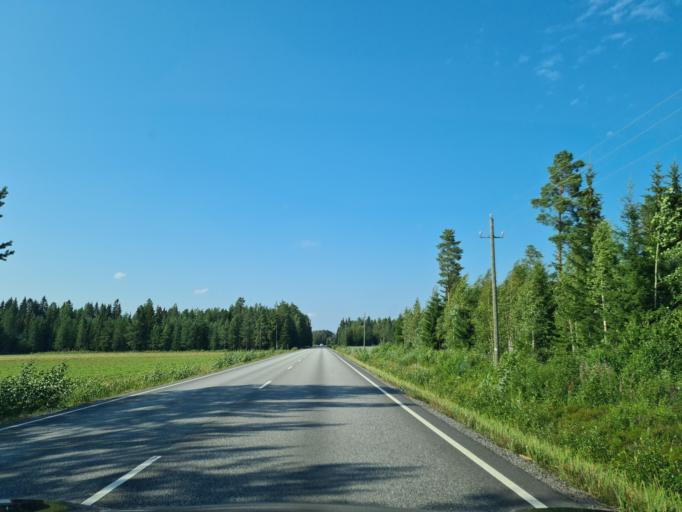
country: FI
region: Satakunta
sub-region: Pohjois-Satakunta
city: Kankaanpaeae
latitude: 61.9300
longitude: 22.5076
